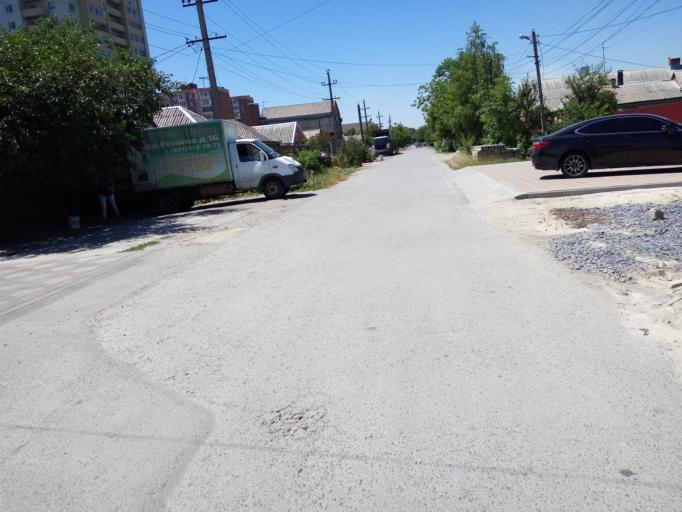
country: RU
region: Rostov
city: Bataysk
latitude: 47.1389
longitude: 39.7702
